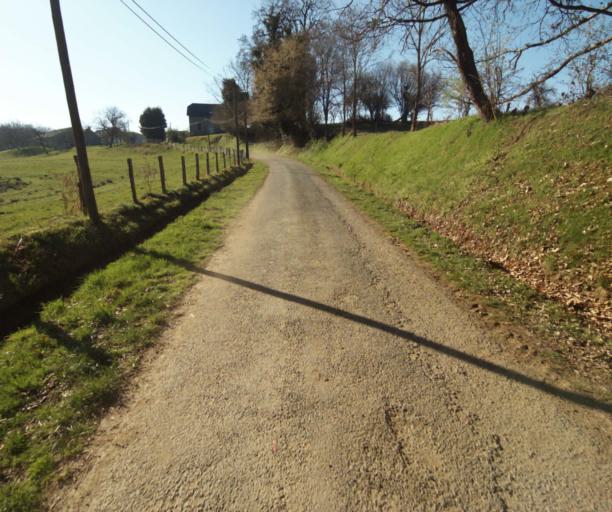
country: FR
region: Limousin
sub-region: Departement de la Correze
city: Saint-Clement
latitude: 45.3769
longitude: 1.6544
